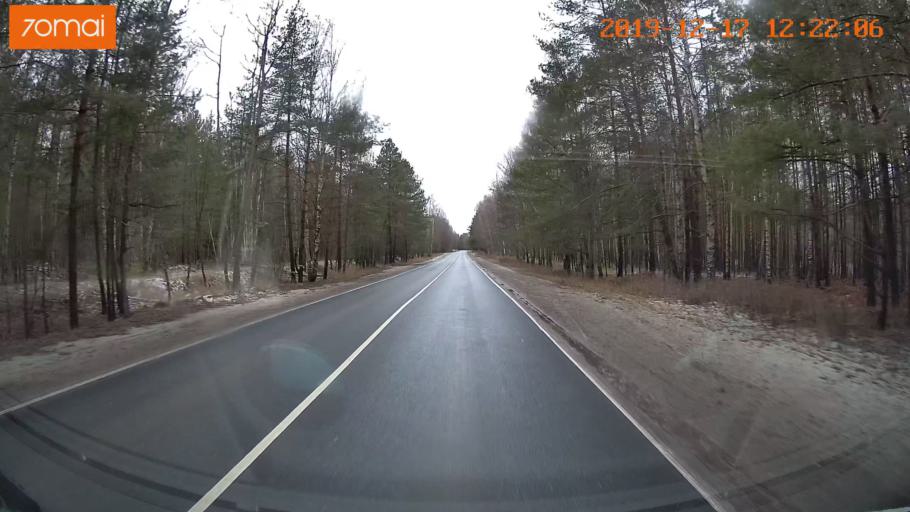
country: RU
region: Rjazan
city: Spas-Klepiki
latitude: 55.1160
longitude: 40.1199
